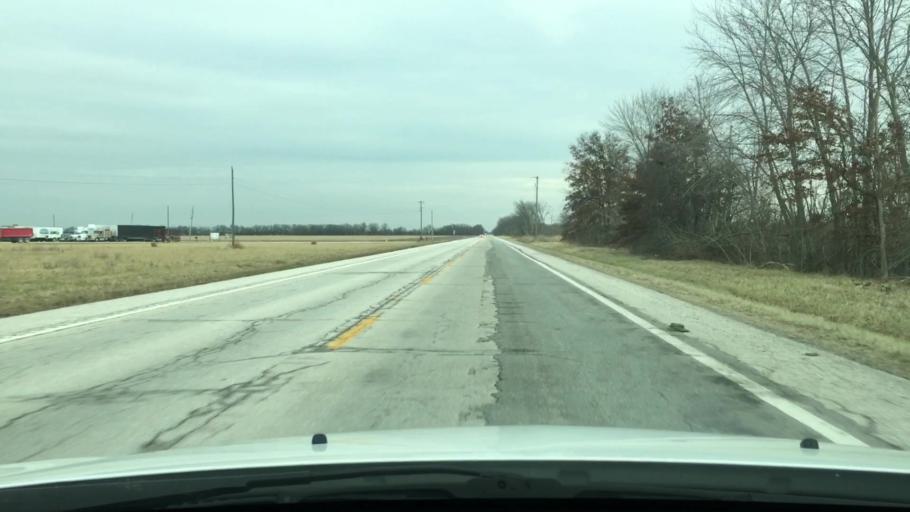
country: US
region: Missouri
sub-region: Audrain County
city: Vandalia
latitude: 39.3202
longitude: -91.4627
